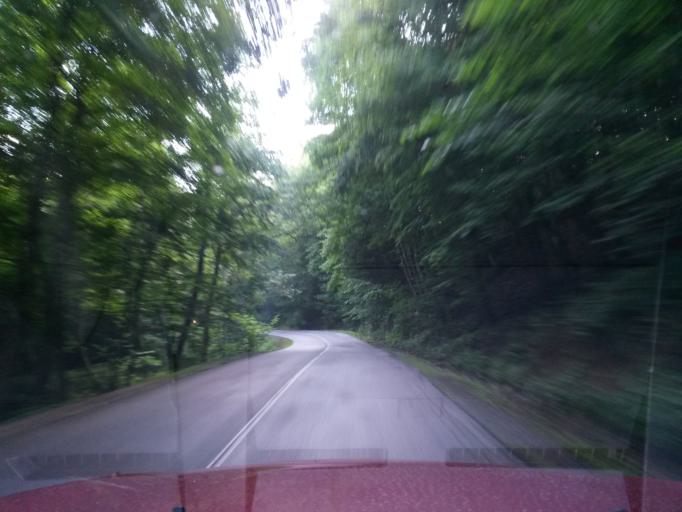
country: SK
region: Kosicky
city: Moldava nad Bodvou
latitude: 48.7250
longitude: 21.0545
